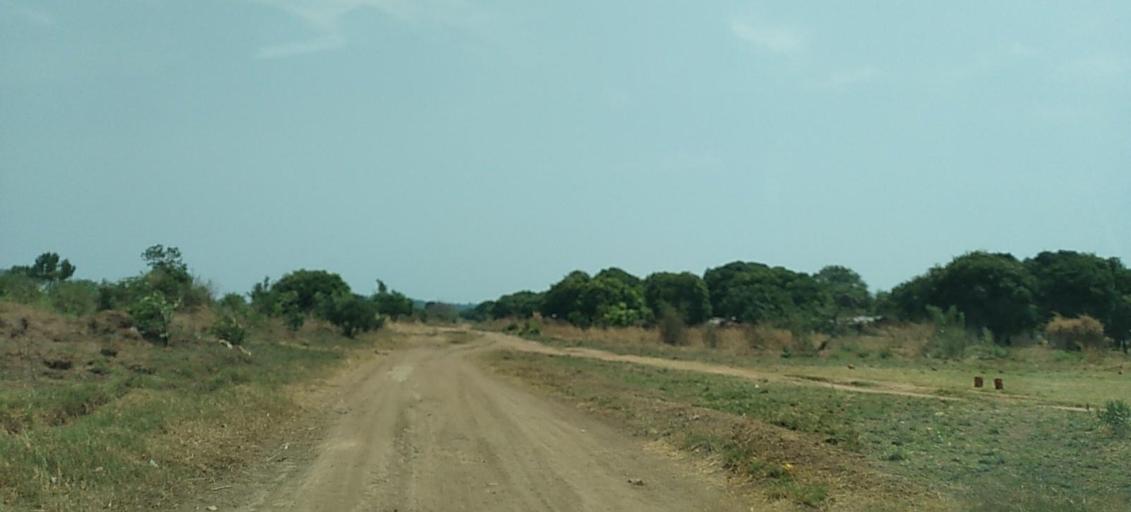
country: ZM
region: Copperbelt
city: Ndola
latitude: -13.0847
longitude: 28.7466
